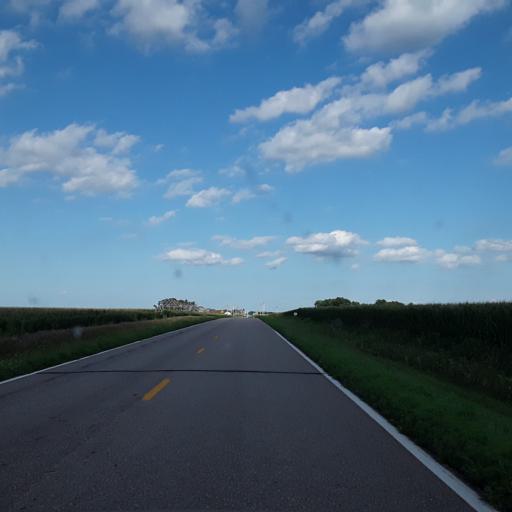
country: US
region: Nebraska
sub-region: Hall County
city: Wood River
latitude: 40.8878
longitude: -98.6146
